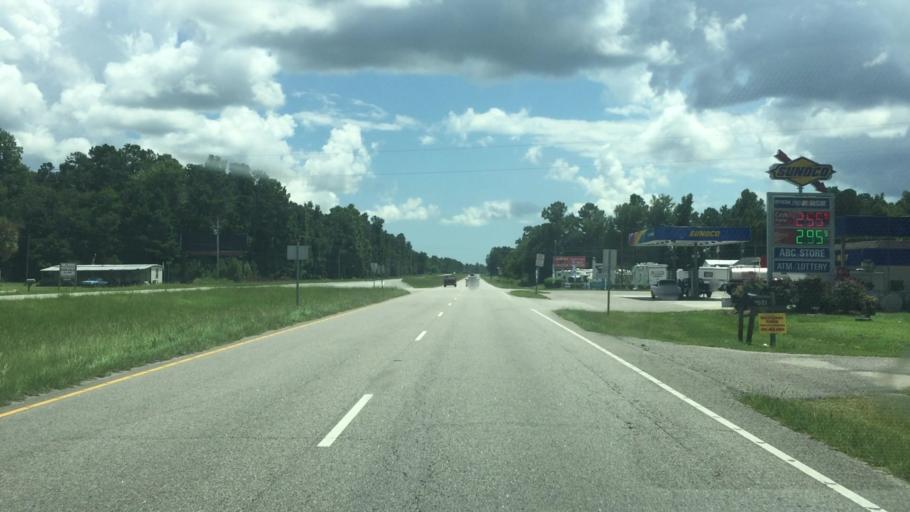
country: US
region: South Carolina
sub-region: Horry County
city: Loris
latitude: 33.9838
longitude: -78.7460
